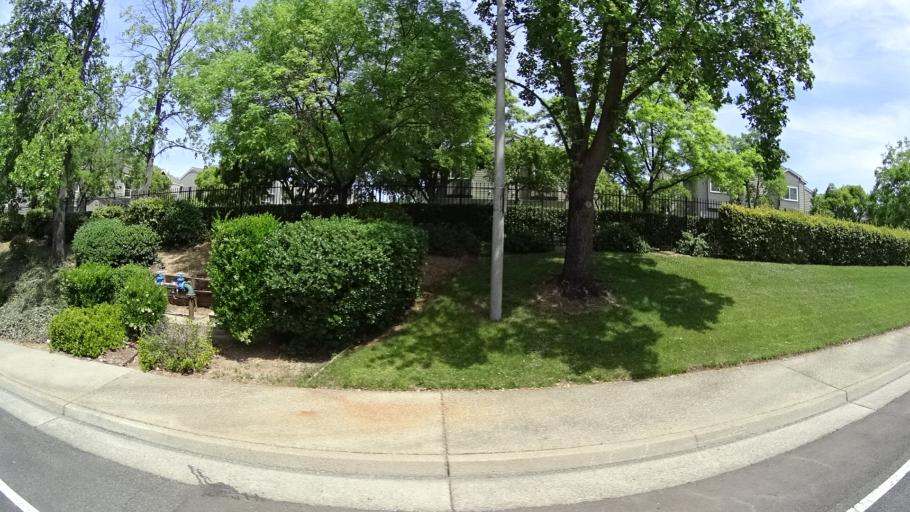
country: US
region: California
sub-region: Placer County
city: Rocklin
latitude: 38.7911
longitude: -121.2589
